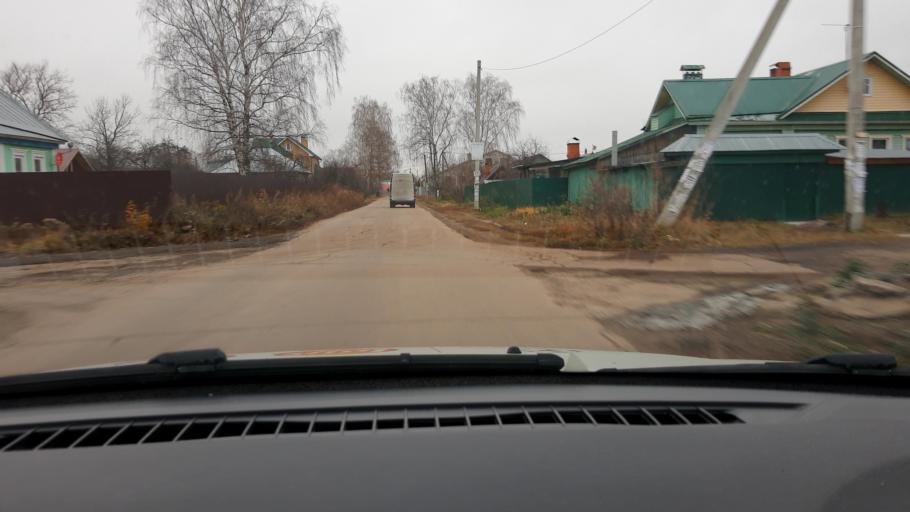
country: RU
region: Nizjnij Novgorod
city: Burevestnik
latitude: 56.2016
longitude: 43.7757
